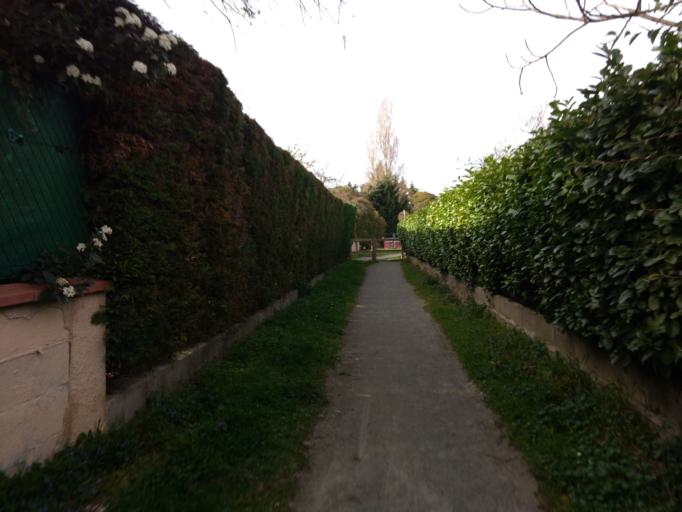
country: FR
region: Midi-Pyrenees
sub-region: Departement de la Haute-Garonne
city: Colomiers
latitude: 43.5851
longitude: 1.3542
